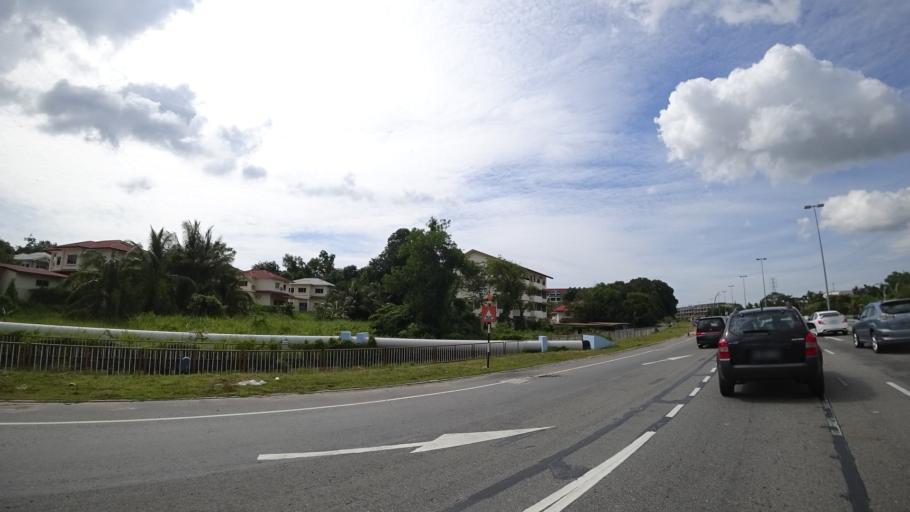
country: BN
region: Brunei and Muara
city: Bandar Seri Begawan
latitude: 4.8844
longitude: 114.8959
